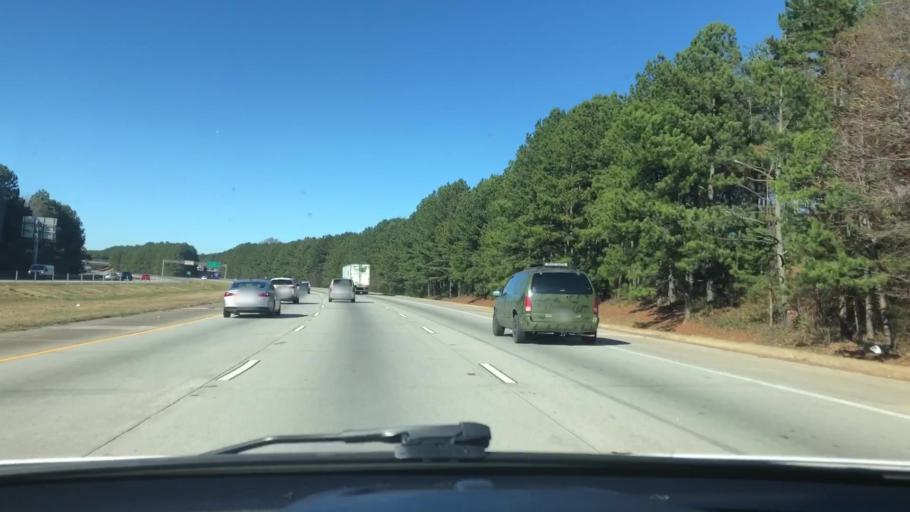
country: US
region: Georgia
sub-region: Clayton County
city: Conley
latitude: 33.6268
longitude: -84.2985
